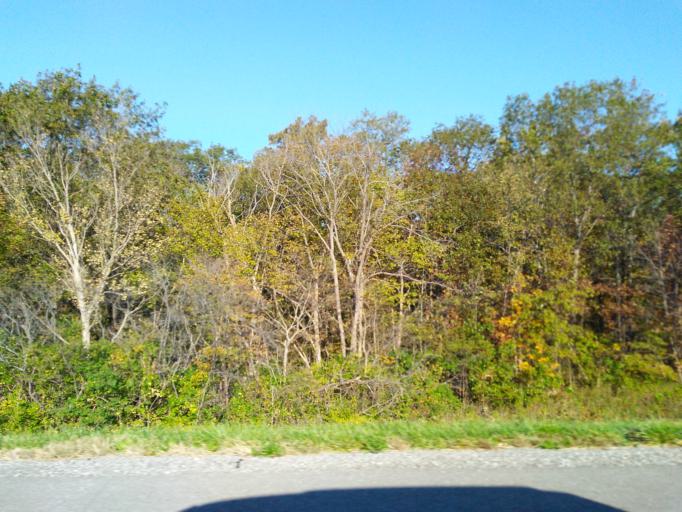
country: US
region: Illinois
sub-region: Madison County
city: Saint Jacob
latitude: 38.7724
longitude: -89.7475
